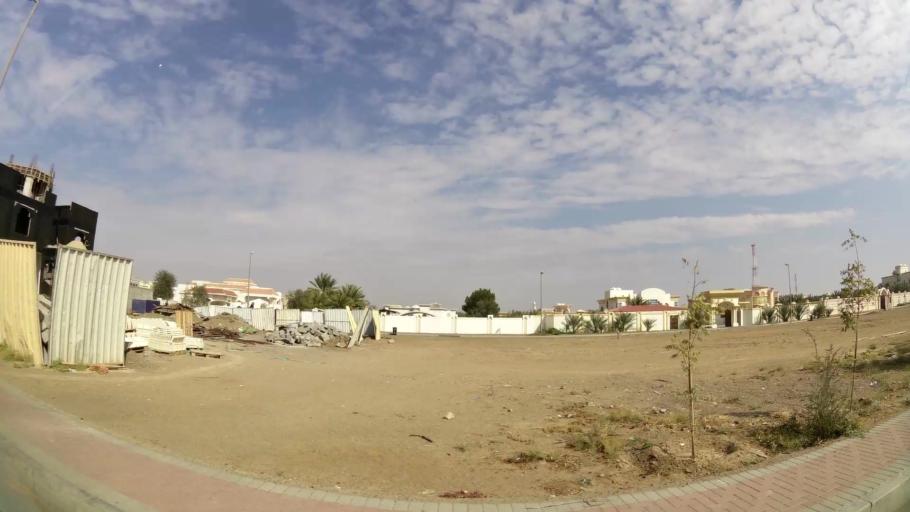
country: AE
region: Abu Dhabi
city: Al Ain
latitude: 24.0974
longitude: 55.9102
